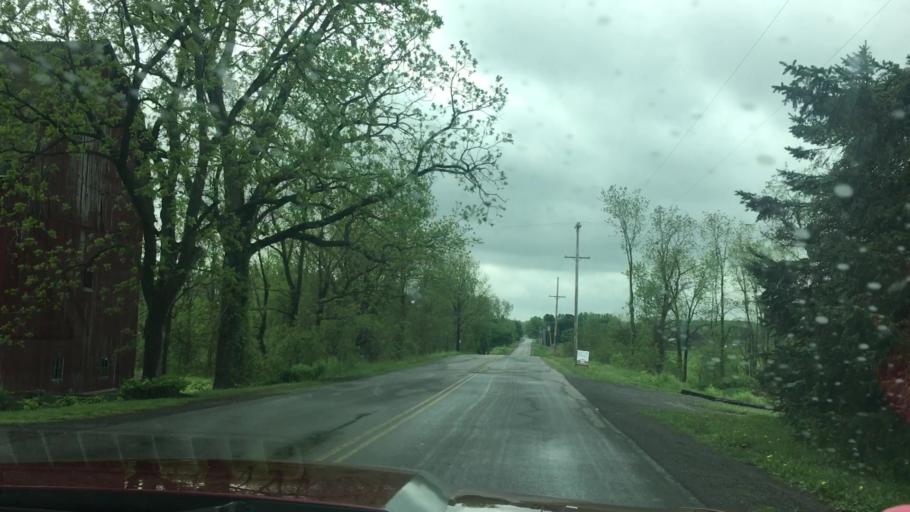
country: US
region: New York
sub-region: Genesee County
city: Batavia
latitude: 43.0803
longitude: -78.1395
